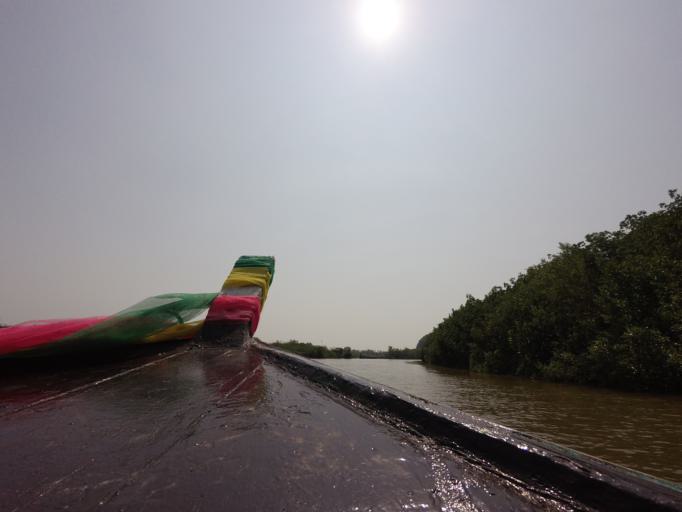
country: TH
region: Prachuap Khiri Khan
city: Kui Buri
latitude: 12.1384
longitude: 99.9609
